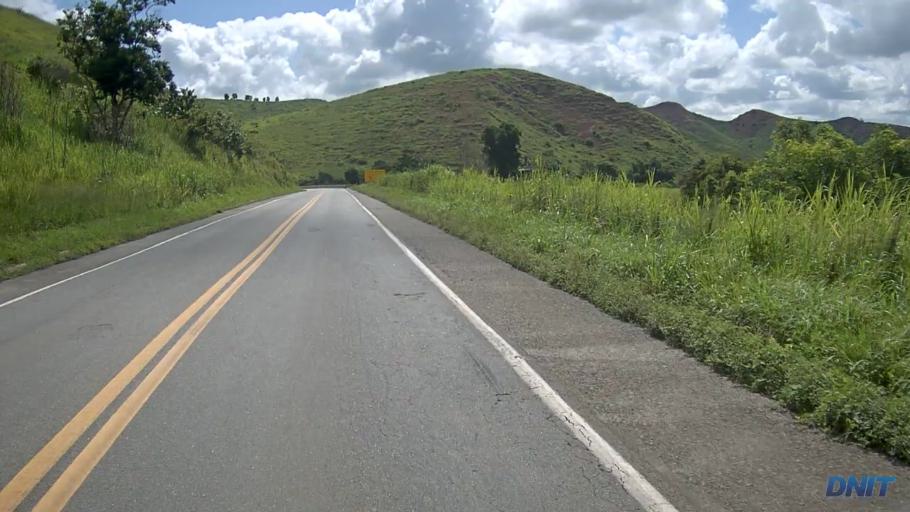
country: BR
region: Minas Gerais
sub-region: Belo Oriente
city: Belo Oriente
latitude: -19.1374
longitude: -42.2165
